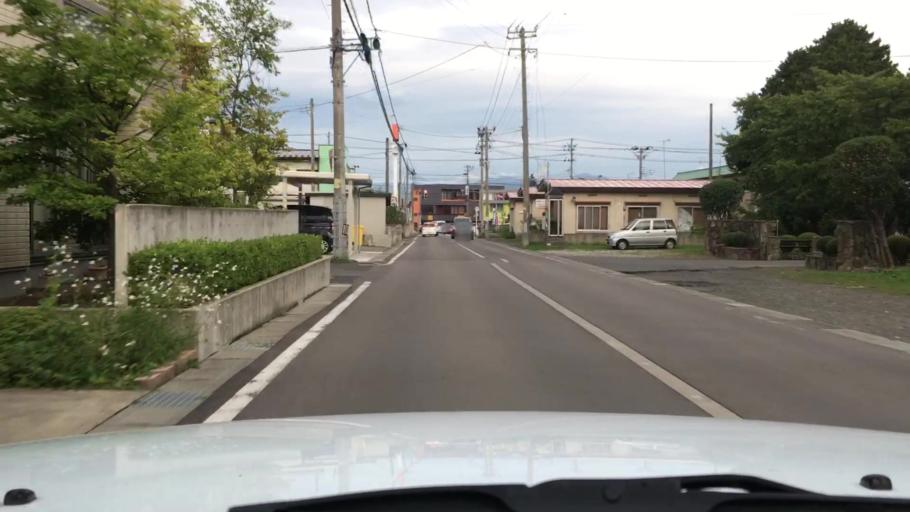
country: JP
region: Aomori
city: Hirosaki
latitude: 40.5936
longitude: 140.4919
